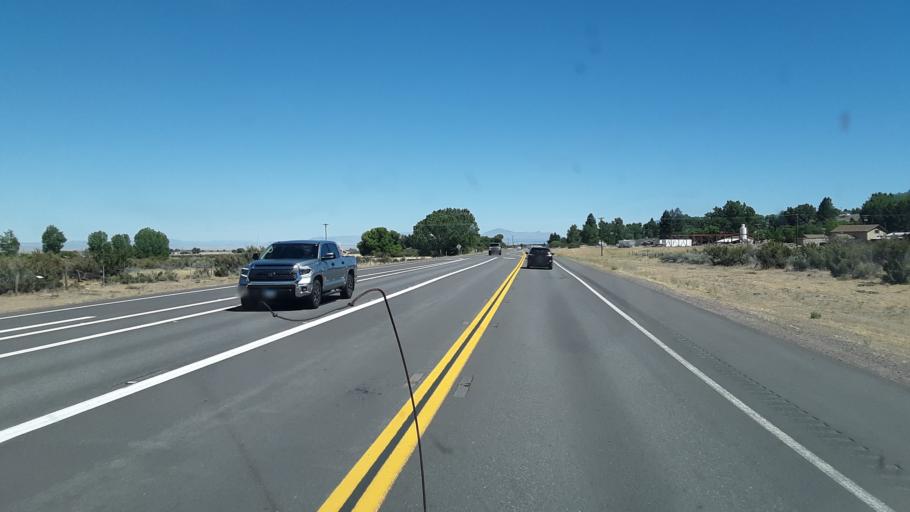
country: US
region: California
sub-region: Lassen County
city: Janesville
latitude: 40.2943
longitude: -120.5081
